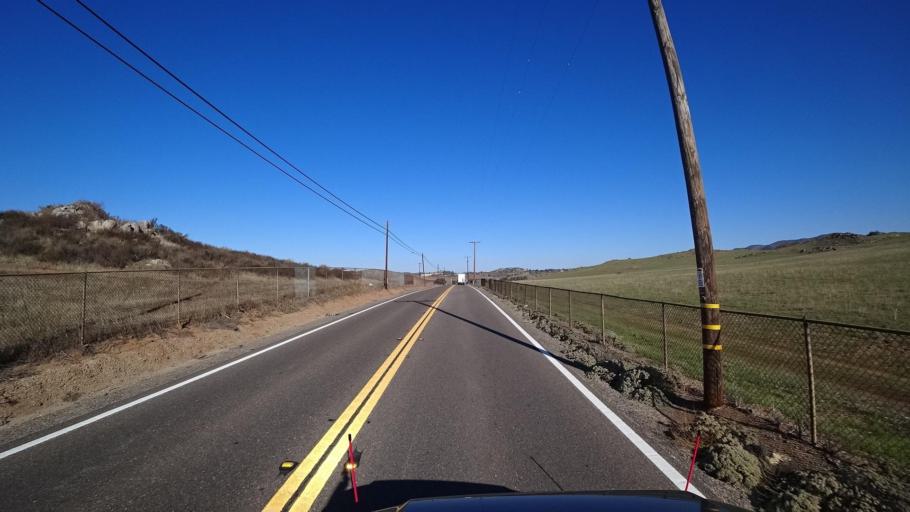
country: US
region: California
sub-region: San Diego County
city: Jamul
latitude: 32.6885
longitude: -116.8525
